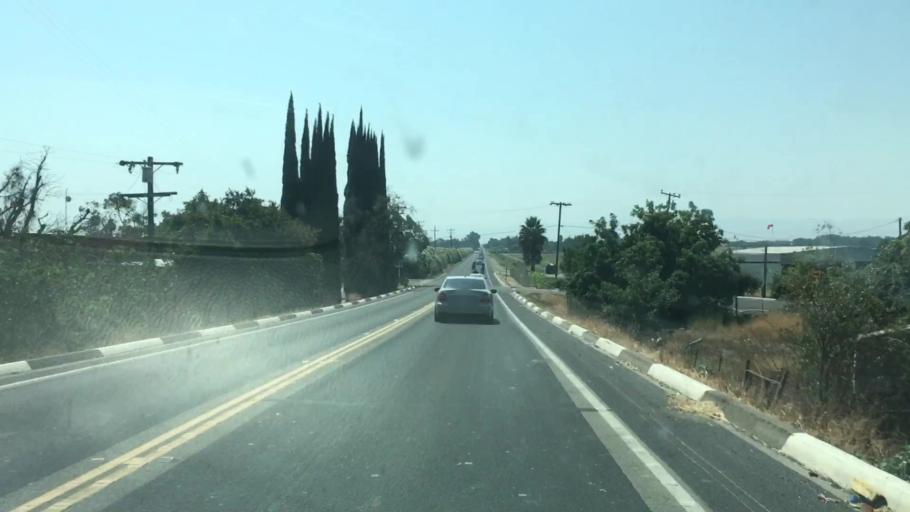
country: US
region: California
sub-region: San Joaquin County
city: Tracy
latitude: 37.8184
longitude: -121.4497
